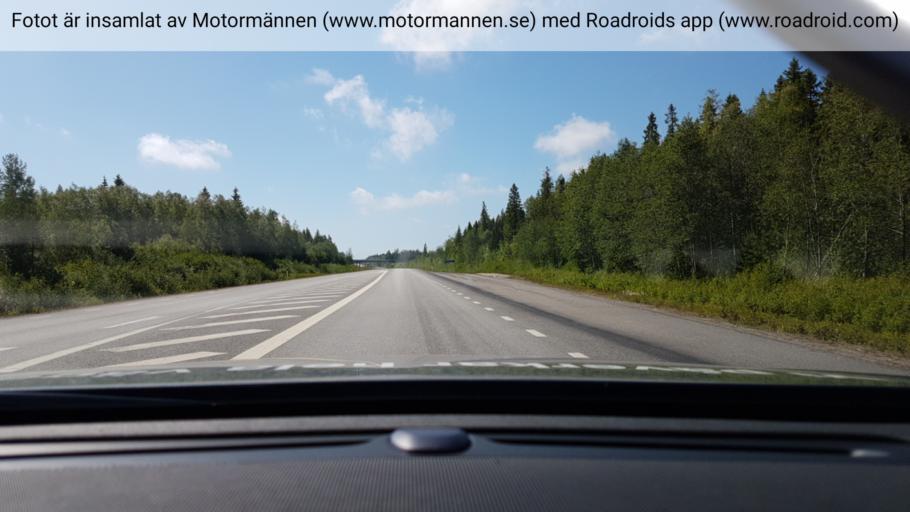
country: SE
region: Vaesterbotten
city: Obbola
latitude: 63.7659
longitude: 20.2958
